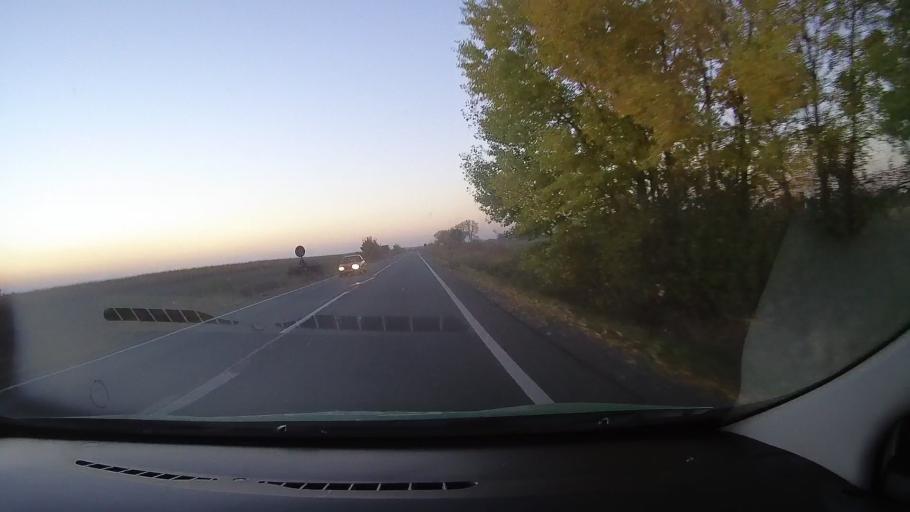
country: RO
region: Bihor
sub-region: Comuna Tarcea
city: Tarcea
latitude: 47.4310
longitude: 22.2072
